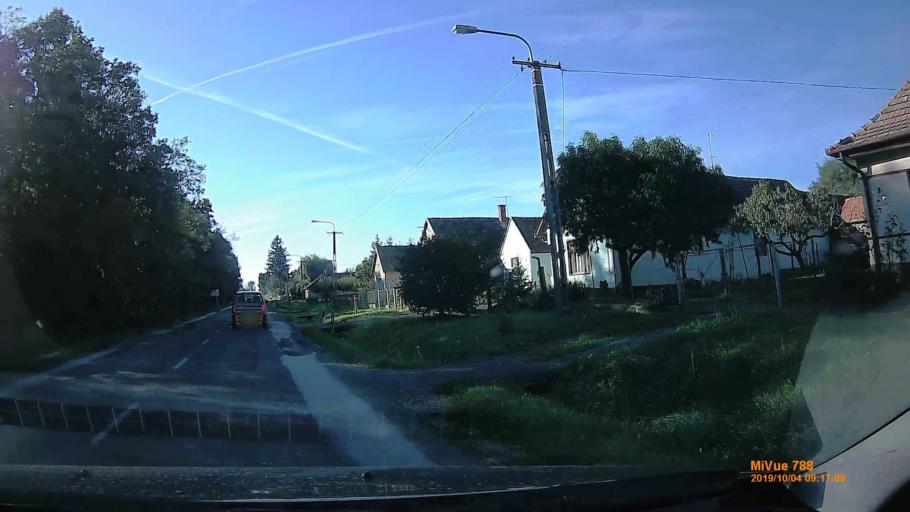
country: HU
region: Somogy
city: Karad
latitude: 46.6051
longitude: 17.7993
